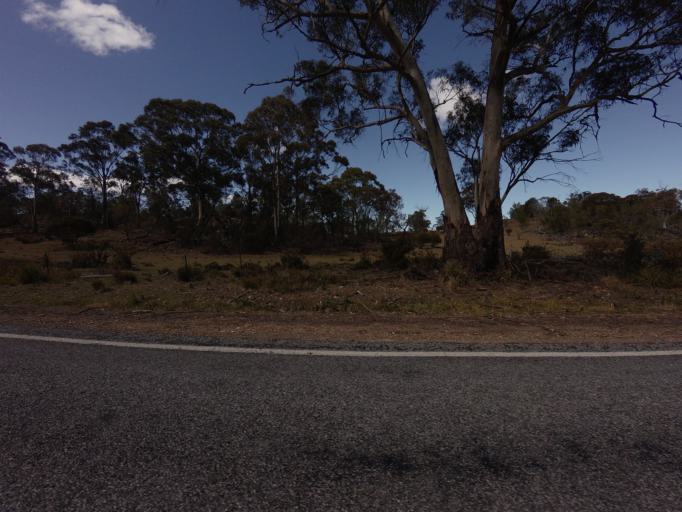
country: AU
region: Tasmania
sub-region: Break O'Day
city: St Helens
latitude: -42.0199
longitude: 148.0067
